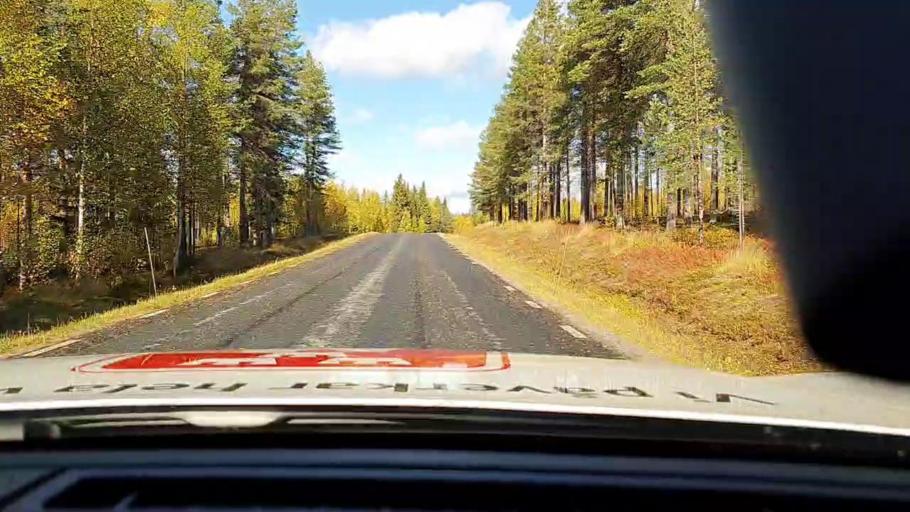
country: SE
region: Vaesterbotten
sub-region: Skelleftea Kommun
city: Langsele
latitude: 65.0168
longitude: 20.0770
